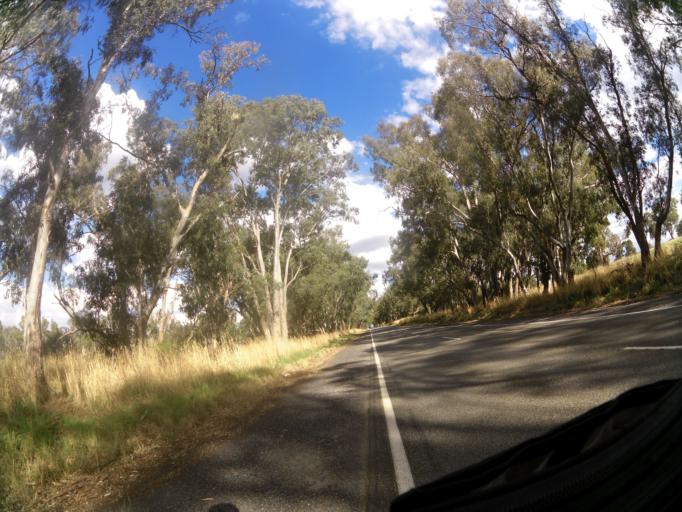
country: AU
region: Victoria
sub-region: Mansfield
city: Mansfield
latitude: -37.0098
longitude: 146.0838
